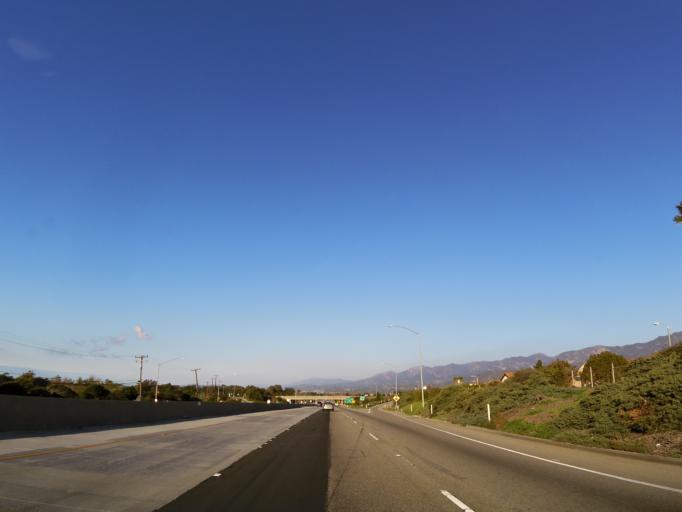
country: US
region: California
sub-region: Santa Barbara County
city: Carpinteria
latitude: 34.3871
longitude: -119.4937
